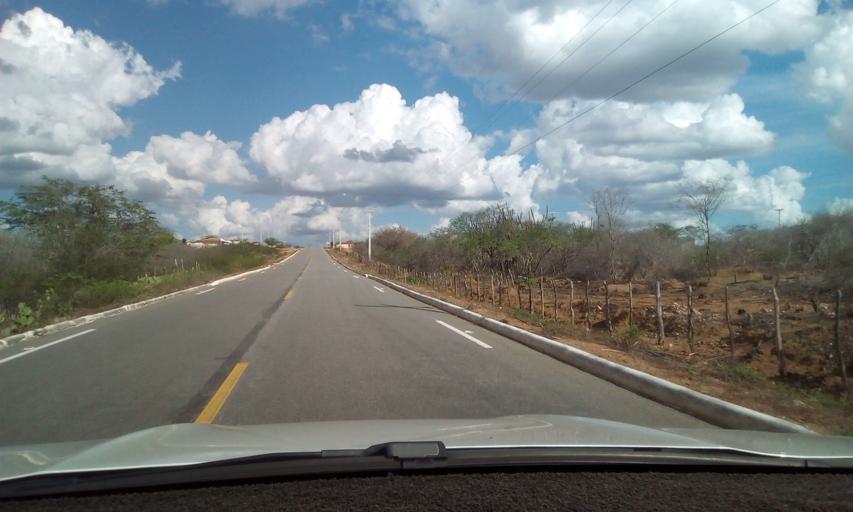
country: BR
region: Paraiba
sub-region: Soledade
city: Soledade
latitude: -6.7957
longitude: -36.4103
